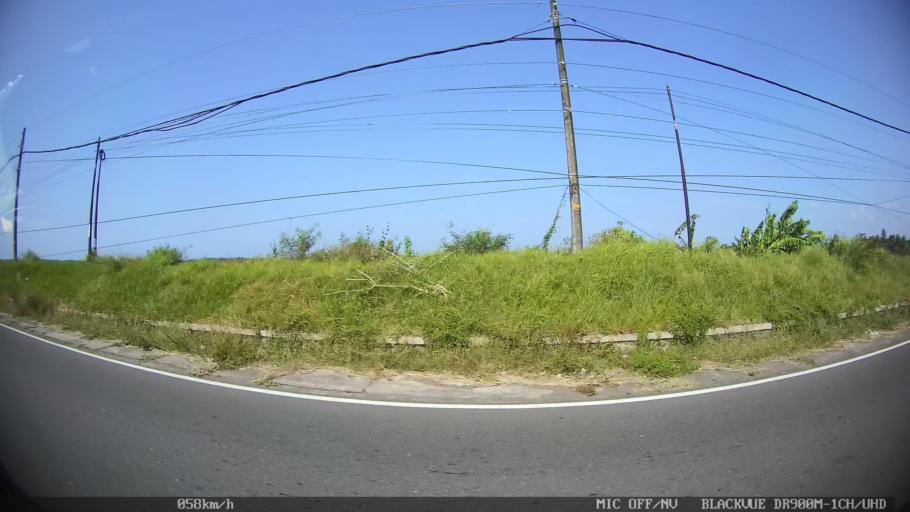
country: ID
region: Daerah Istimewa Yogyakarta
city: Srandakan
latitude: -7.9267
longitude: 110.1891
